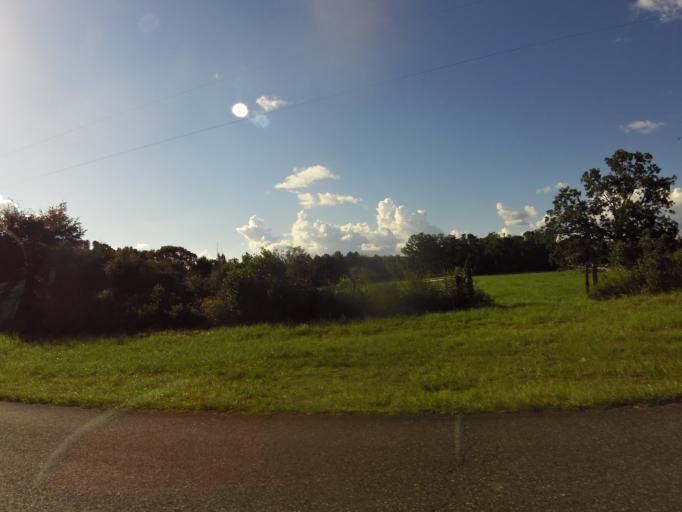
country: US
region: Florida
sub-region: Wakulla County
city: Crawfordville
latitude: 30.0641
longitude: -84.5179
